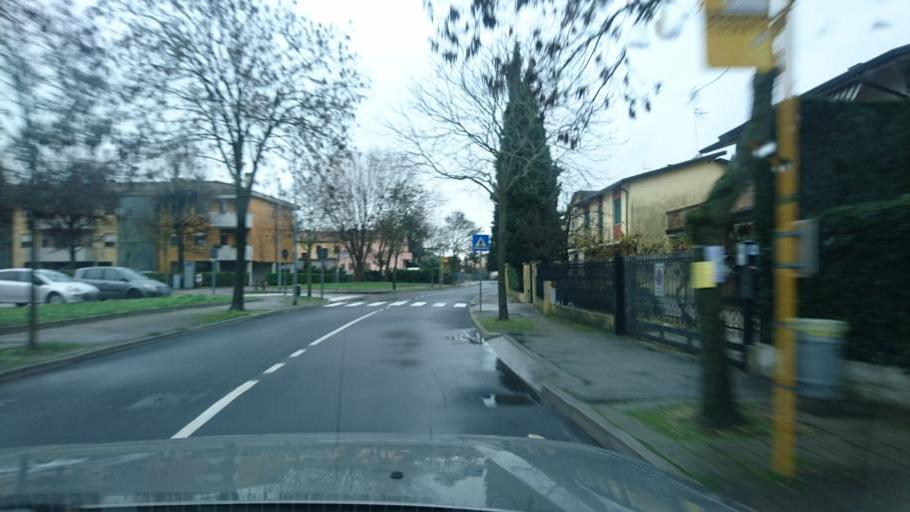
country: IT
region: Veneto
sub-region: Provincia di Padova
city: Ponte San Nicolo
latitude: 45.3767
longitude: 11.9391
